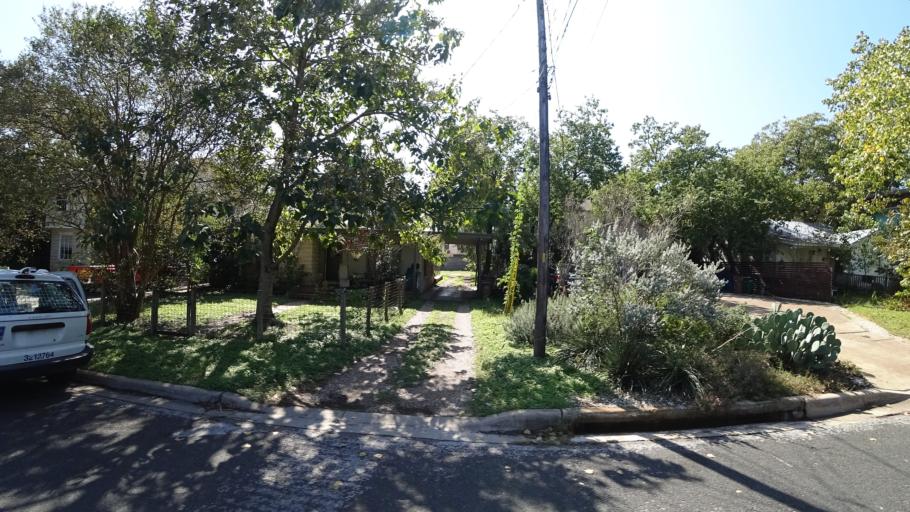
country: US
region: Texas
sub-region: Travis County
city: Austin
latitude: 30.2534
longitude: -97.7686
